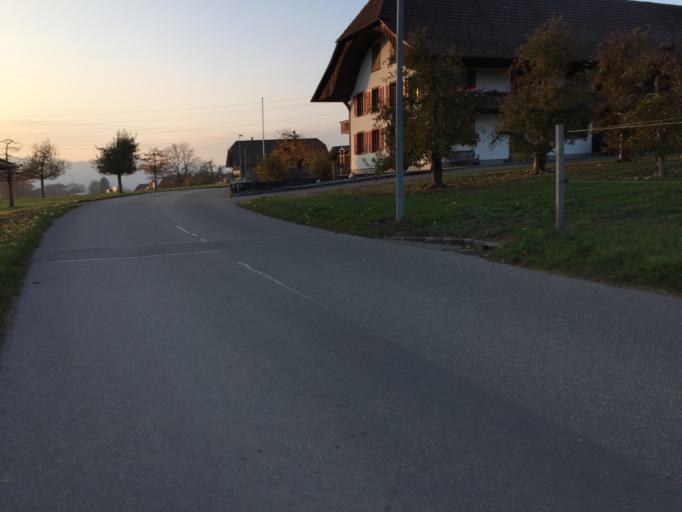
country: CH
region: Bern
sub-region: Bern-Mittelland District
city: Taegertschi
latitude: 46.8772
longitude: 7.5837
